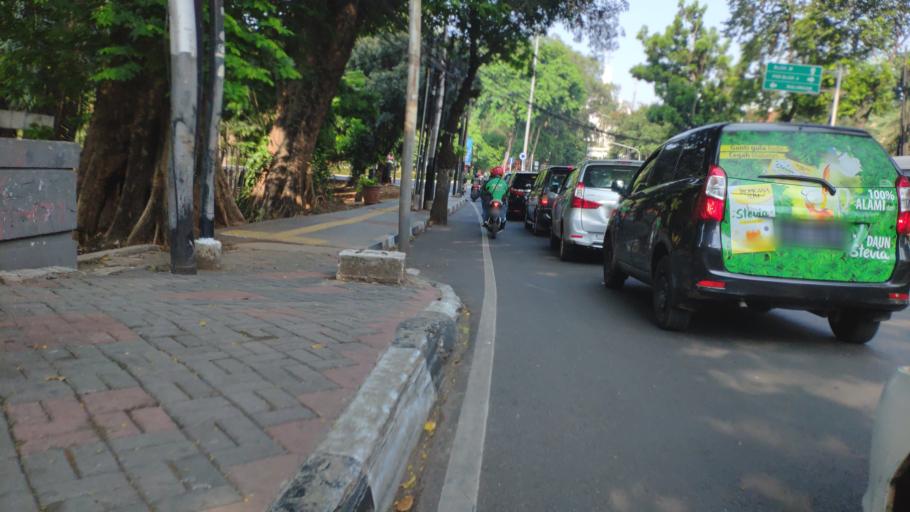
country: ID
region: Jakarta Raya
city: Jakarta
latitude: -6.2461
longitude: 106.7937
